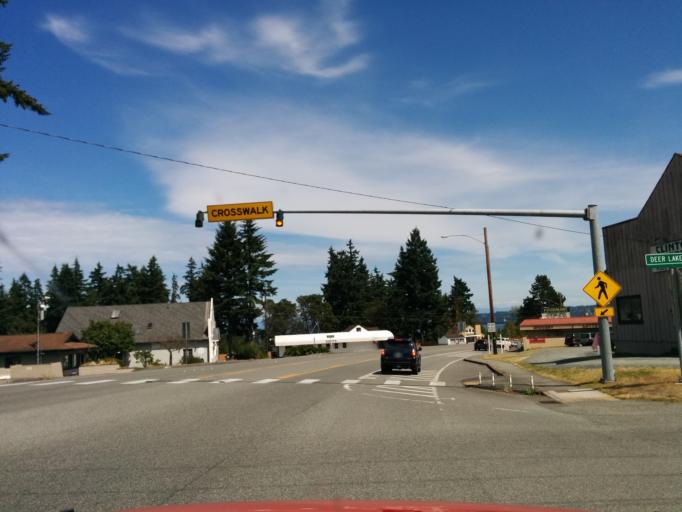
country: US
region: Washington
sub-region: Snohomish County
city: Mukilteo
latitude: 47.9796
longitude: -122.3583
